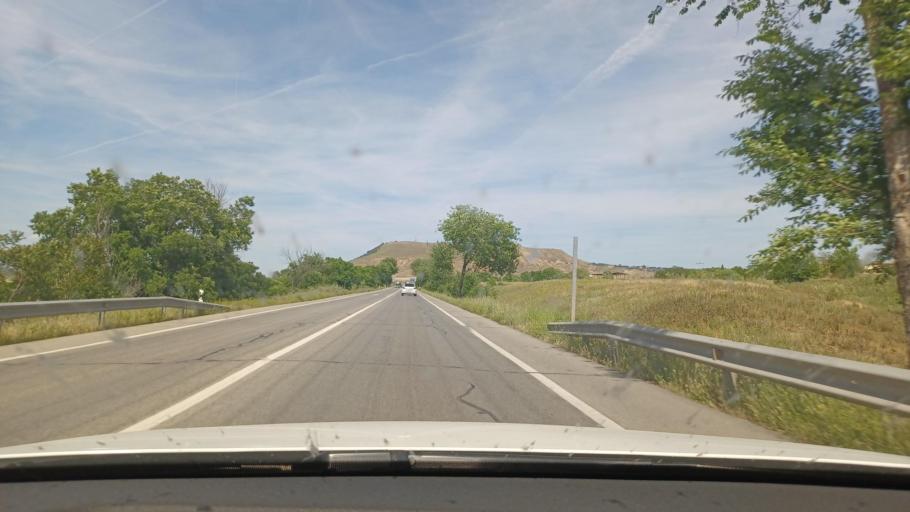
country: ES
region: Madrid
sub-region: Provincia de Madrid
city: Torrejon de Ardoz
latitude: 40.4358
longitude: -3.4351
